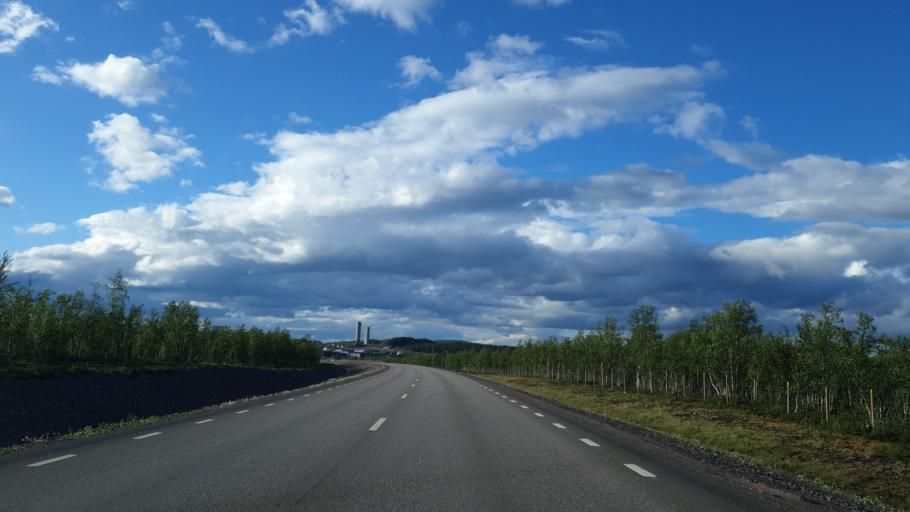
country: SE
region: Norrbotten
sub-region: Kiruna Kommun
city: Kiruna
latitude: 67.8343
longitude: 20.3072
